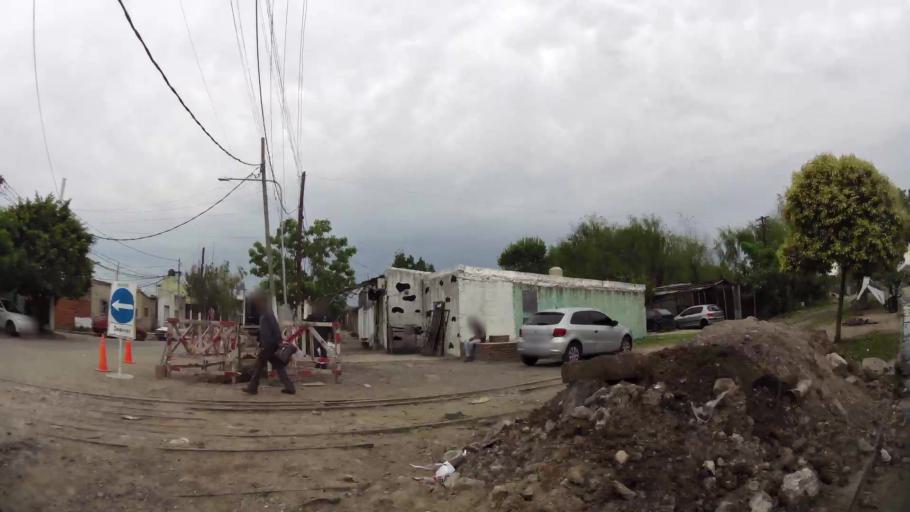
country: AR
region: Buenos Aires
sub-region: Partido de Avellaneda
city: Avellaneda
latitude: -34.6511
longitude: -58.3585
